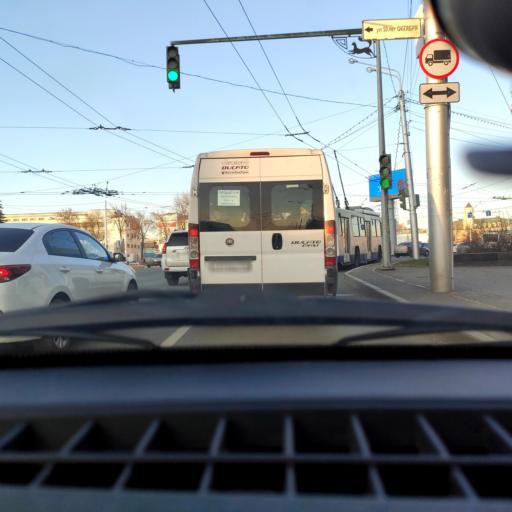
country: RU
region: Bashkortostan
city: Ufa
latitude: 54.7382
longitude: 55.9820
